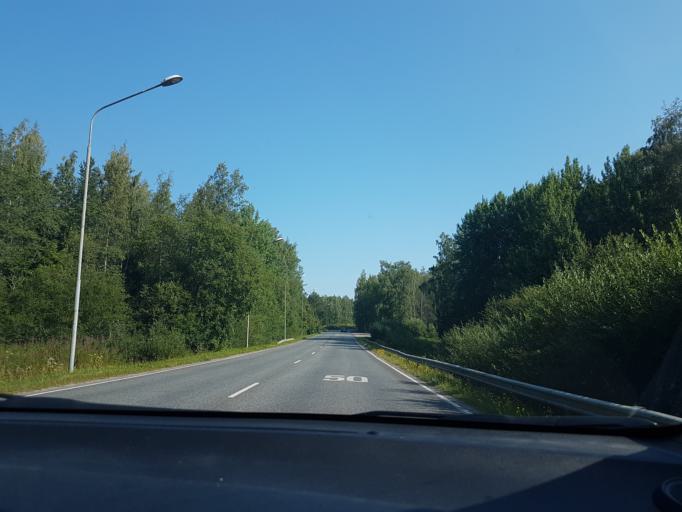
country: FI
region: Uusimaa
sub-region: Helsinki
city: Kerava
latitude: 60.3842
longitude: 25.0983
